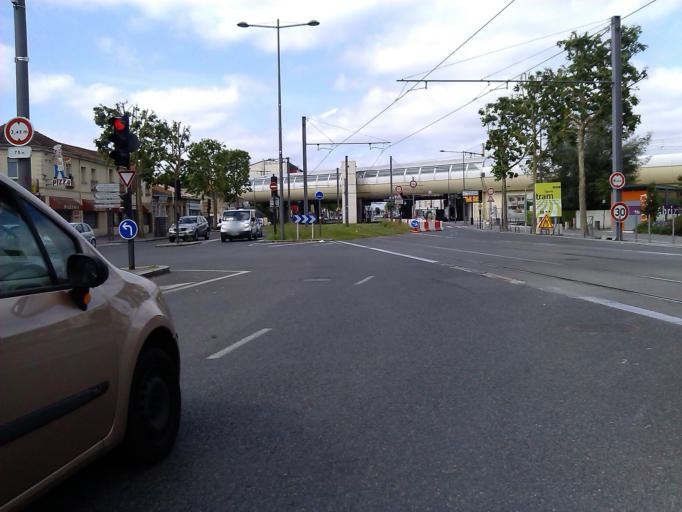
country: FR
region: Aquitaine
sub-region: Departement de la Gironde
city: Cenon
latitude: 44.8574
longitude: -0.5320
